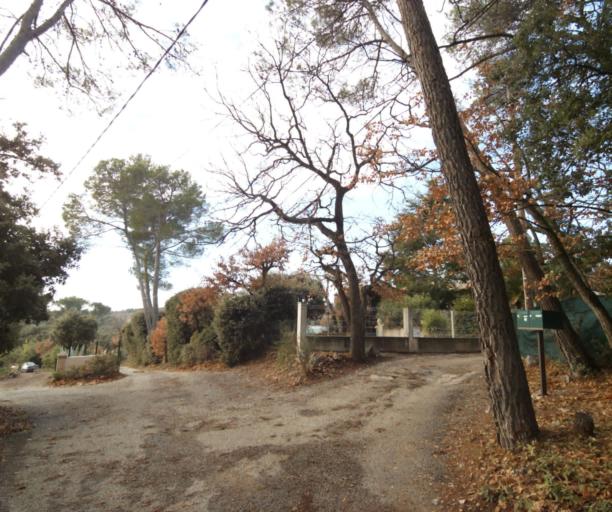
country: FR
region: Provence-Alpes-Cote d'Azur
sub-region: Departement du Var
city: Trans-en-Provence
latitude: 43.4864
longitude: 6.4995
